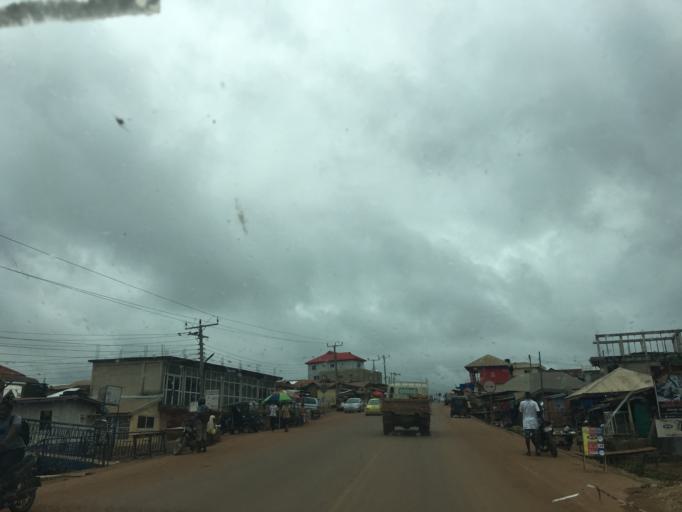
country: GH
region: Western
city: Wassa-Akropong
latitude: 5.8094
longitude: -2.4382
